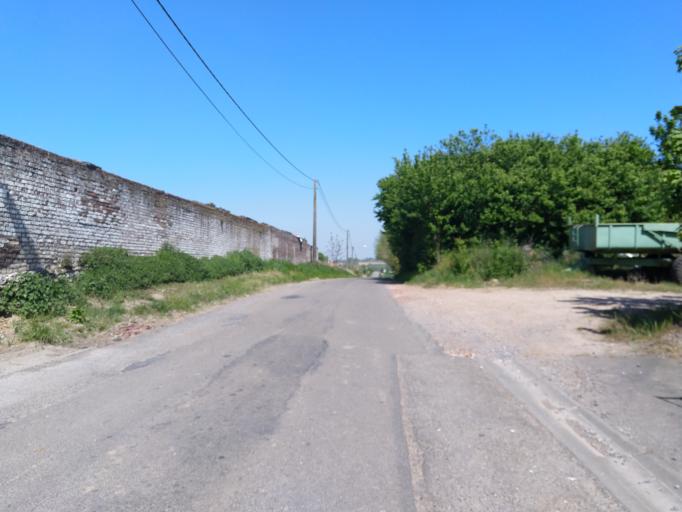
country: BE
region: Wallonia
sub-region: Province du Hainaut
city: Soignies
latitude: 50.6100
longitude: 4.0075
